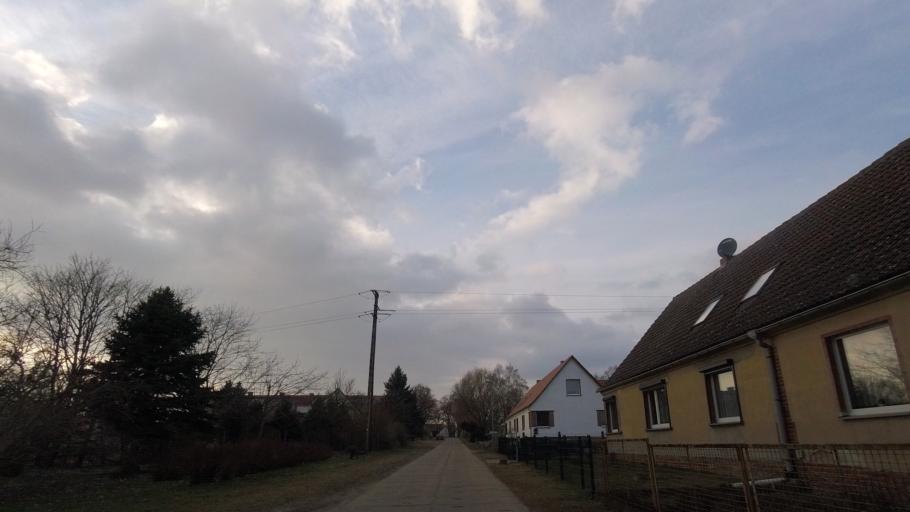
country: DE
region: Brandenburg
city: Belzig
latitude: 52.1386
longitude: 12.5226
